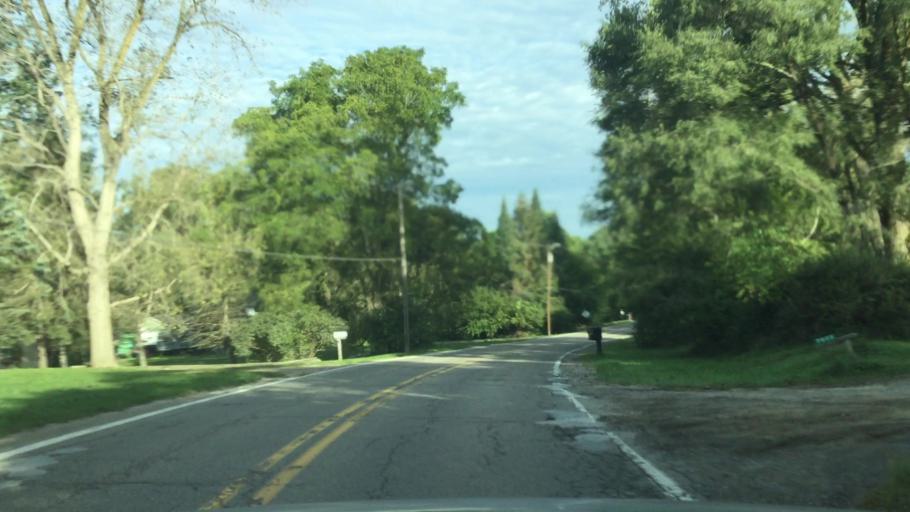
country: US
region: Michigan
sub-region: Livingston County
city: Brighton
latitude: 42.4845
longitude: -83.8509
